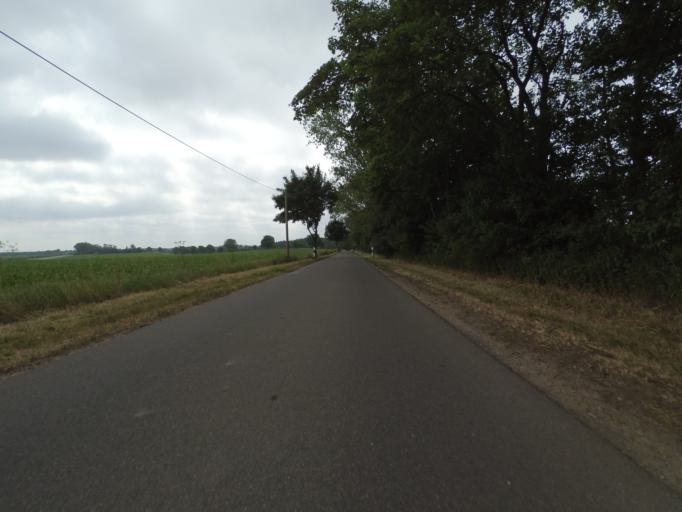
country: DE
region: Mecklenburg-Vorpommern
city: Krakow am See
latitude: 53.6400
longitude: 12.3365
